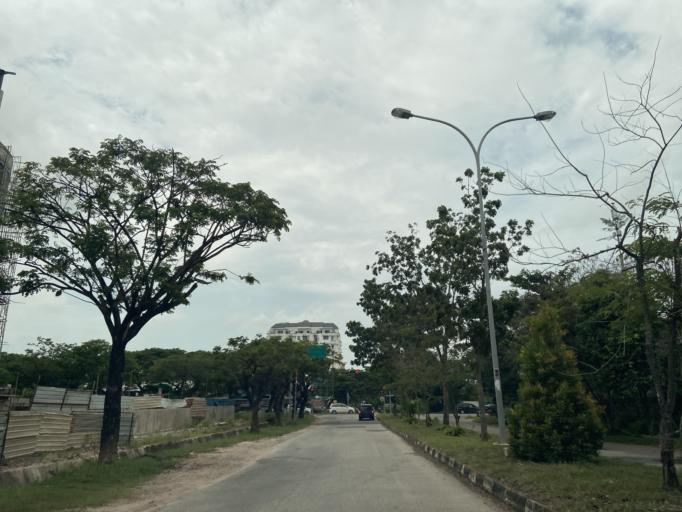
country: SG
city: Singapore
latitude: 1.1294
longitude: 104.0467
